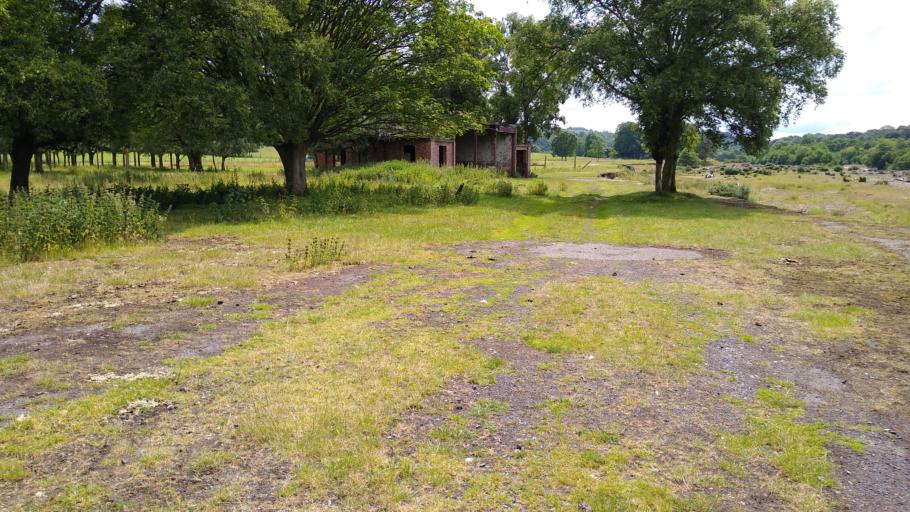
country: GB
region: England
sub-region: Northumberland
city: Greenhead
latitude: 54.9370
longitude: -2.5126
